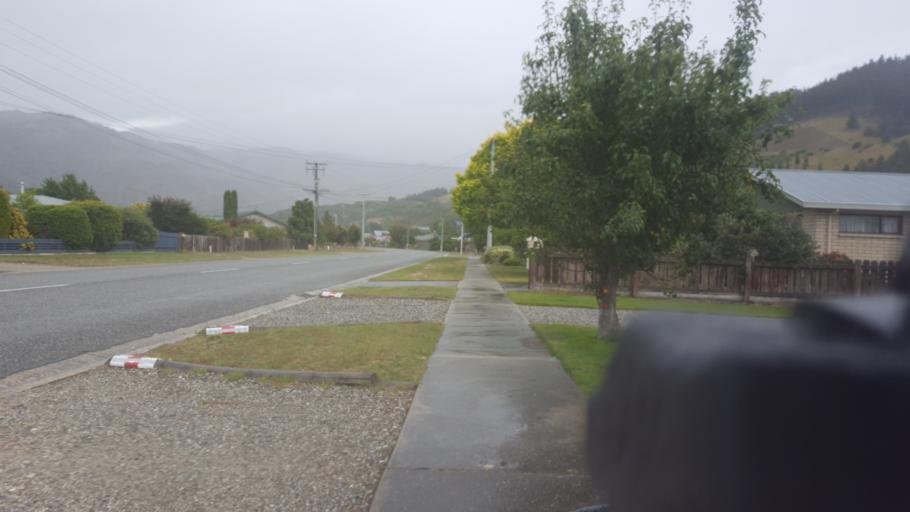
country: NZ
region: Otago
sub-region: Queenstown-Lakes District
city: Wanaka
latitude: -45.1889
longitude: 169.3255
